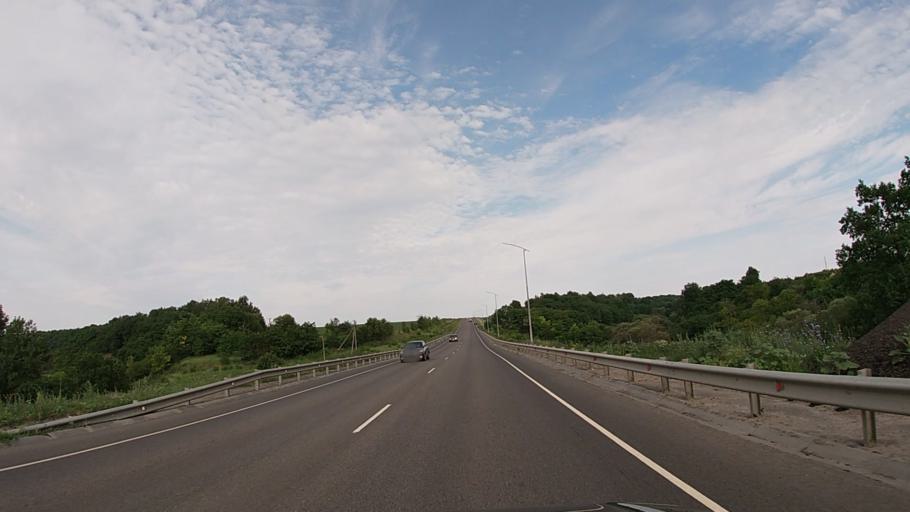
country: RU
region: Belgorod
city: Severnyy
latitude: 50.6644
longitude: 36.5209
